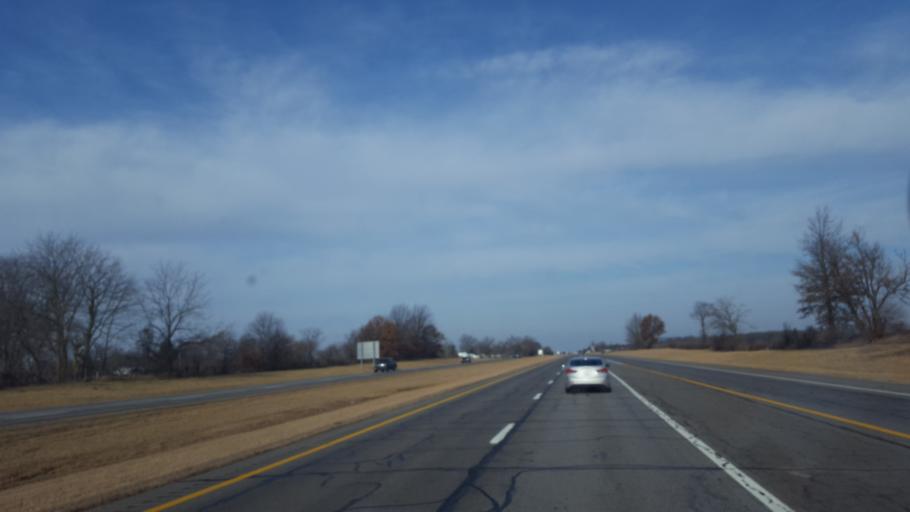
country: US
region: Ohio
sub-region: Marion County
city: Marion
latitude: 40.6939
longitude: -83.1526
